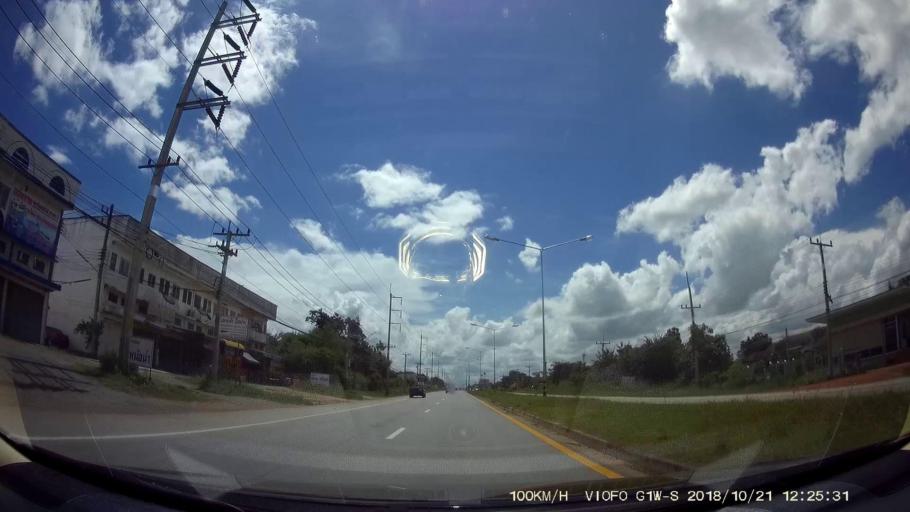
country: TH
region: Nakhon Ratchasima
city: Dan Khun Thot
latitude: 15.2201
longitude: 101.7714
